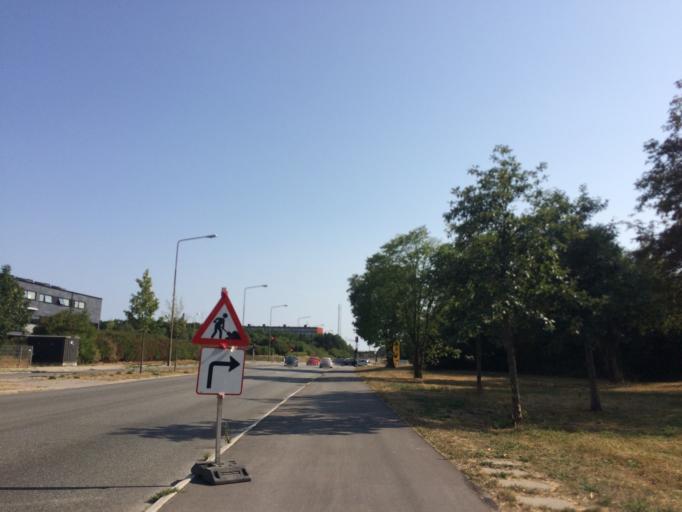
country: DK
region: Capital Region
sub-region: Hvidovre Kommune
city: Hvidovre
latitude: 55.6290
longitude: 12.4561
